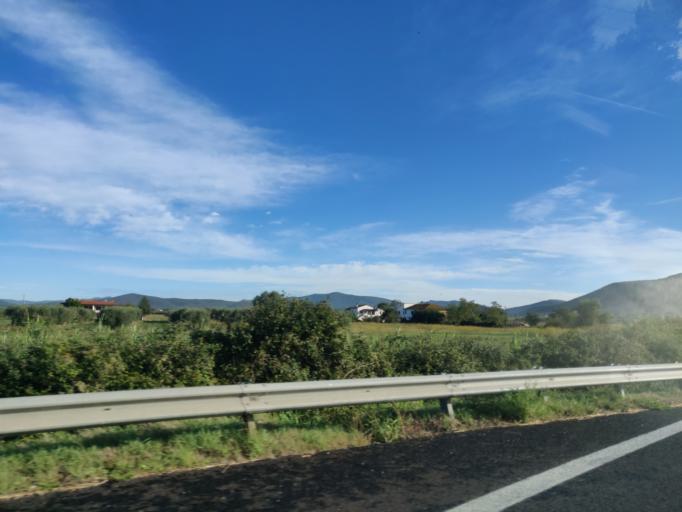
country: IT
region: Tuscany
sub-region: Provincia di Grosseto
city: Bagno Roselle
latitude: 42.7966
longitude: 11.1173
